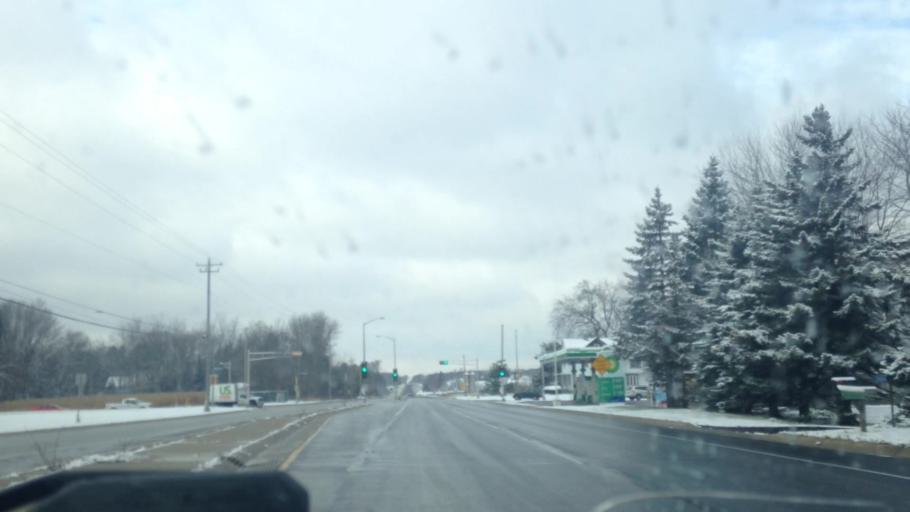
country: US
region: Wisconsin
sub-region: Waukesha County
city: Lannon
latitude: 43.1926
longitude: -88.1806
